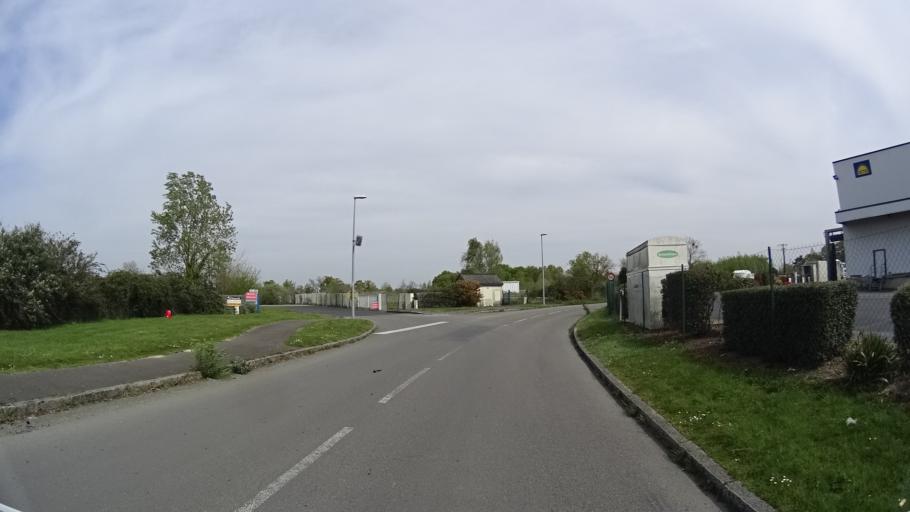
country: FR
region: Brittany
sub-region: Departement d'Ille-et-Vilaine
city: Bruz
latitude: 48.0347
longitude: -1.7328
